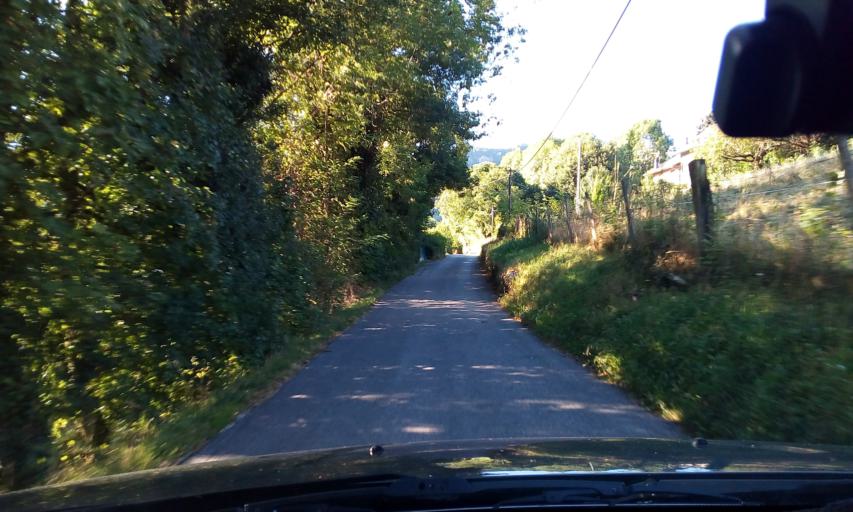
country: FR
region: Rhone-Alpes
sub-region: Departement de la Savoie
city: Barberaz
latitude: 45.5506
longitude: 5.9360
